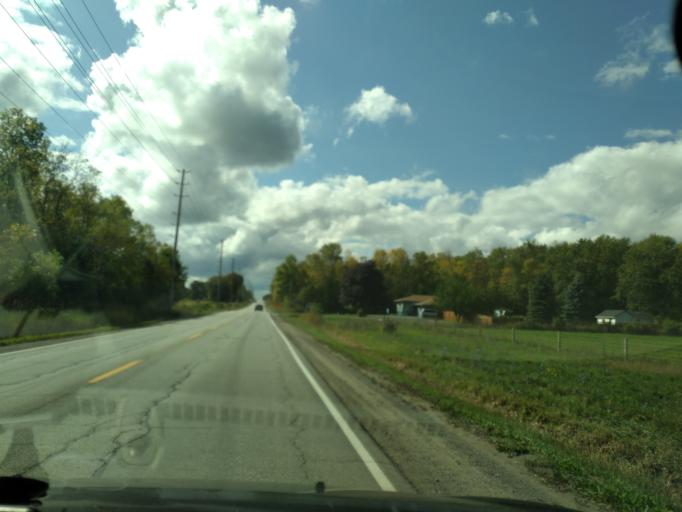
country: CA
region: Ontario
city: Innisfil
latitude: 44.3053
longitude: -79.5904
